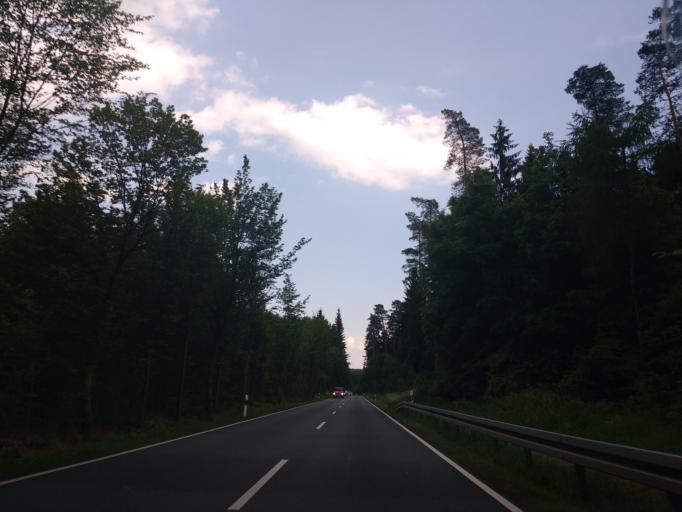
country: DE
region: Hesse
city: Frankenberg
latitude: 51.0122
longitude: 8.8185
